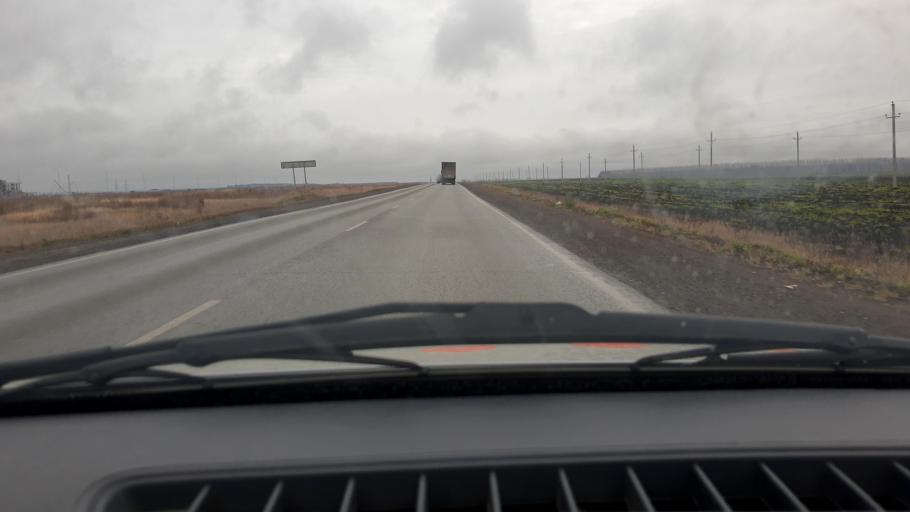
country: RU
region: Bashkortostan
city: Iglino
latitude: 54.7607
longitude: 56.2720
